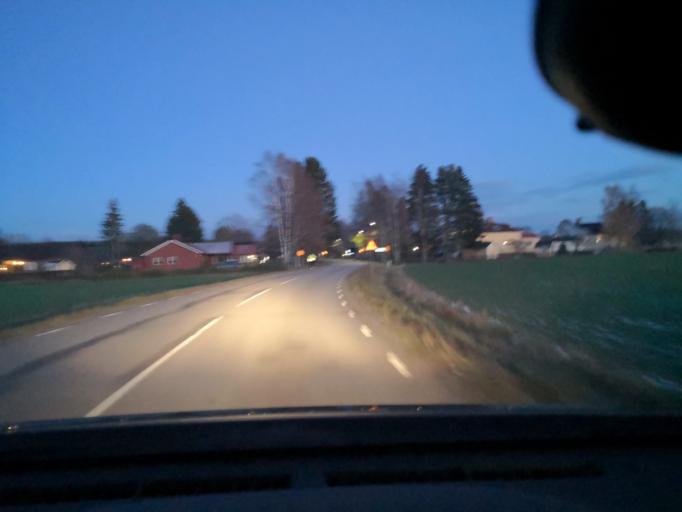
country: SE
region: Vaestmanland
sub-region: Sala Kommun
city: Sala
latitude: 59.8708
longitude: 16.7170
